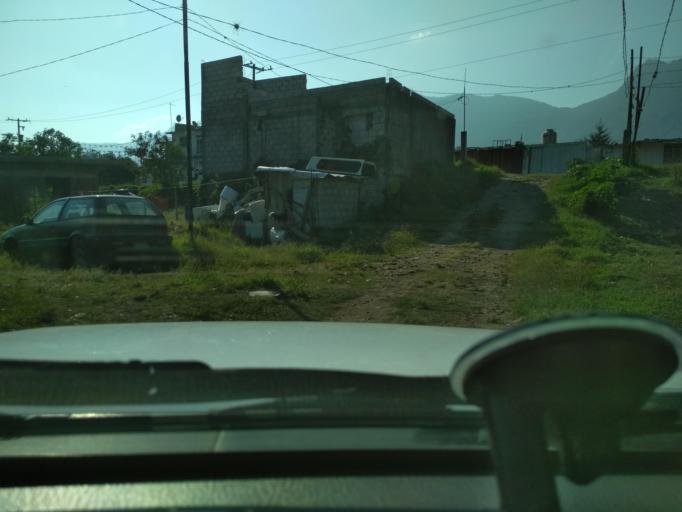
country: MX
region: Veracruz
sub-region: Nogales
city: Agricola Lazaro Cardenas
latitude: 18.8075
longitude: -97.1984
